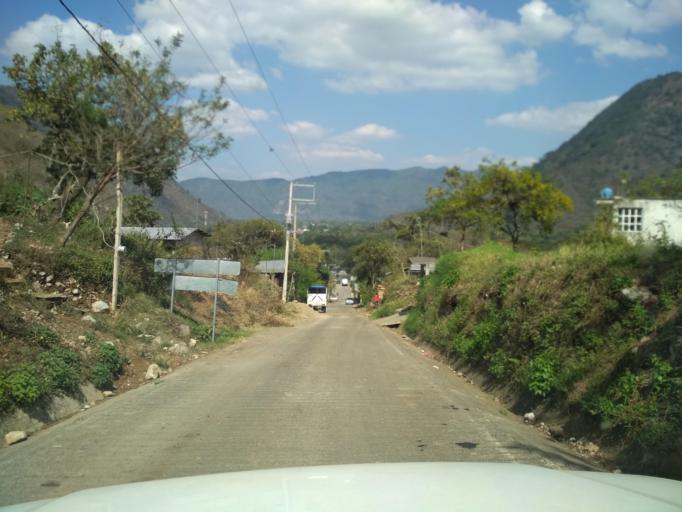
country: MX
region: Veracruz
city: Jalapilla
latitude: 18.8007
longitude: -97.1086
